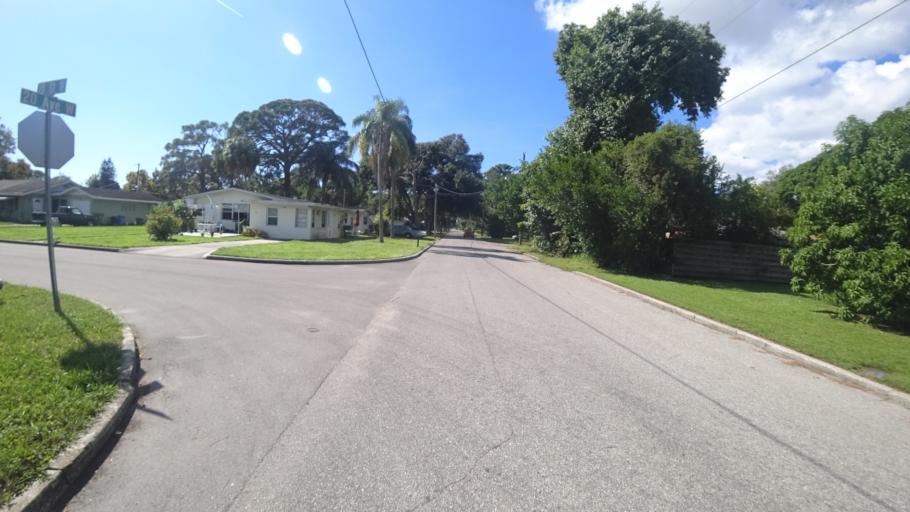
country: US
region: Florida
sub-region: Manatee County
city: Bradenton
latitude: 27.4818
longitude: -82.5810
